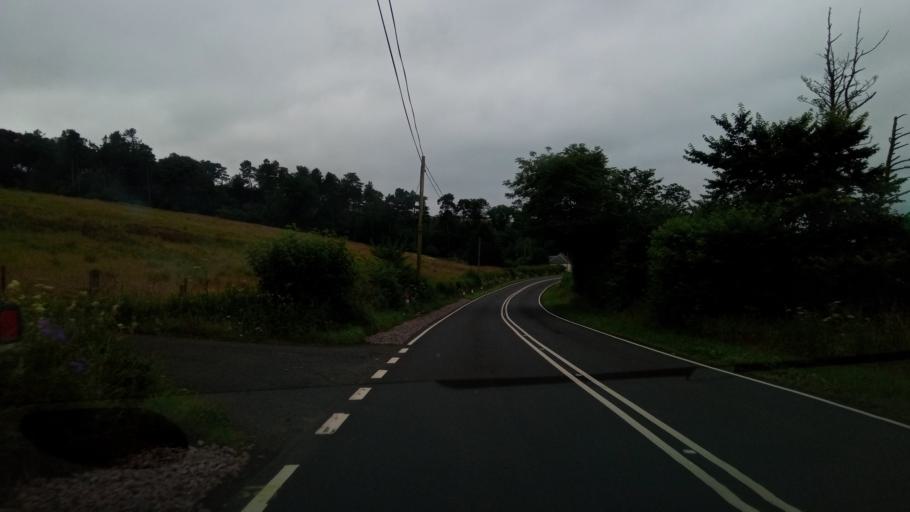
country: GB
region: Scotland
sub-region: The Scottish Borders
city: Hawick
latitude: 55.3481
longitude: -2.9203
